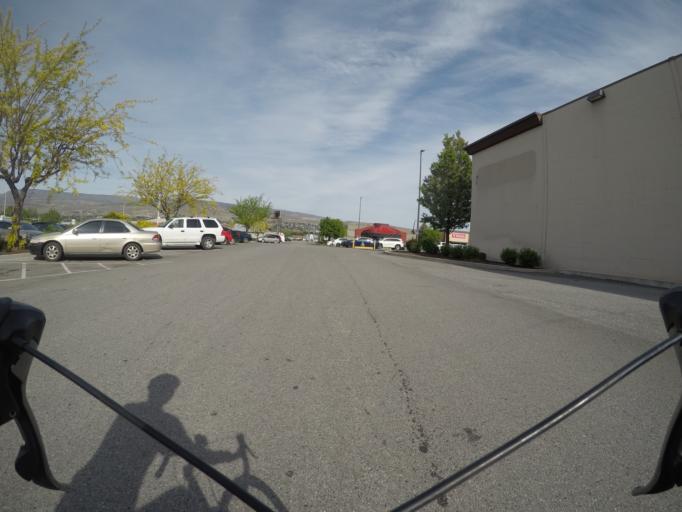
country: US
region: Washington
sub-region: Chelan County
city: Wenatchee
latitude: 47.4411
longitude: -120.3273
